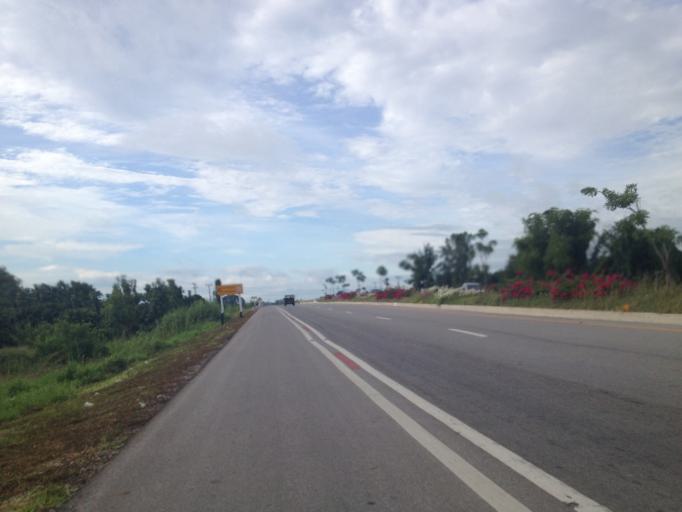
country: TH
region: Chiang Mai
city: San Pa Tong
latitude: 18.5597
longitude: 98.8499
